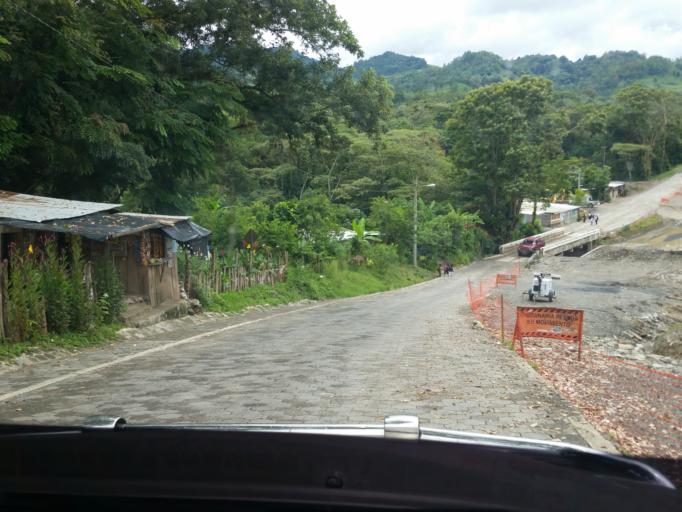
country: NI
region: Jinotega
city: Jinotega
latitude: 13.1806
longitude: -85.9111
